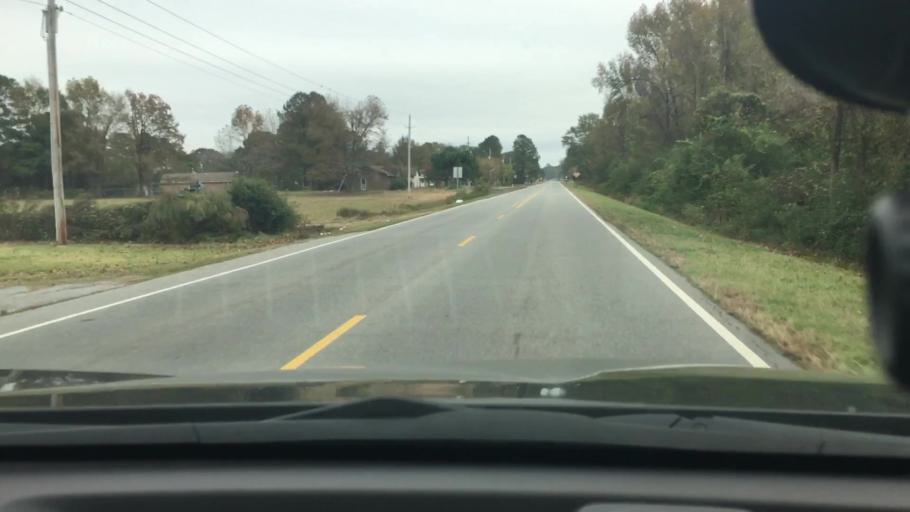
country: US
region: North Carolina
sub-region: Pitt County
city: Greenville
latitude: 35.6318
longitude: -77.3563
